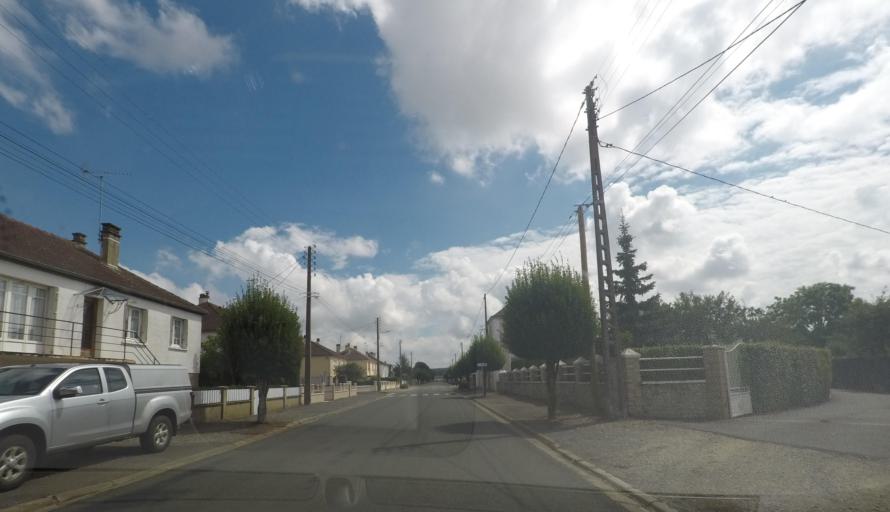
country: FR
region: Pays de la Loire
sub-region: Departement de la Sarthe
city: Saint-Cosme-en-Vairais
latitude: 48.2725
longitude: 0.4664
